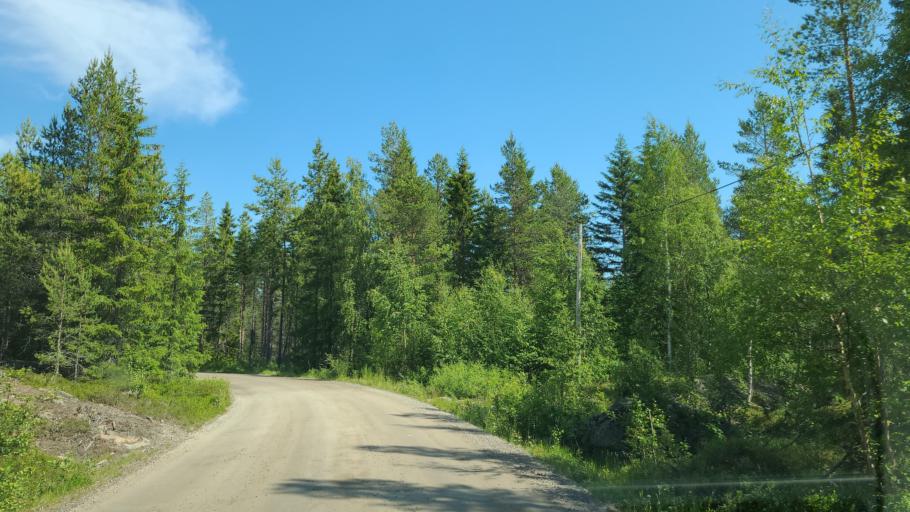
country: SE
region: Vaesterbotten
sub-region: Robertsfors Kommun
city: Robertsfors
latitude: 64.1580
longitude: 20.9413
